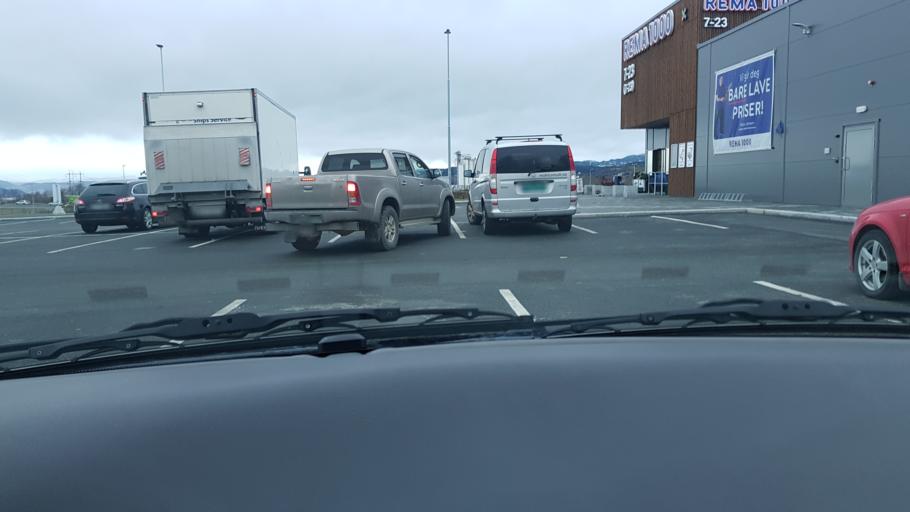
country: NO
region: Sor-Trondelag
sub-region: Melhus
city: Melhus
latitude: 63.3340
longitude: 10.3608
